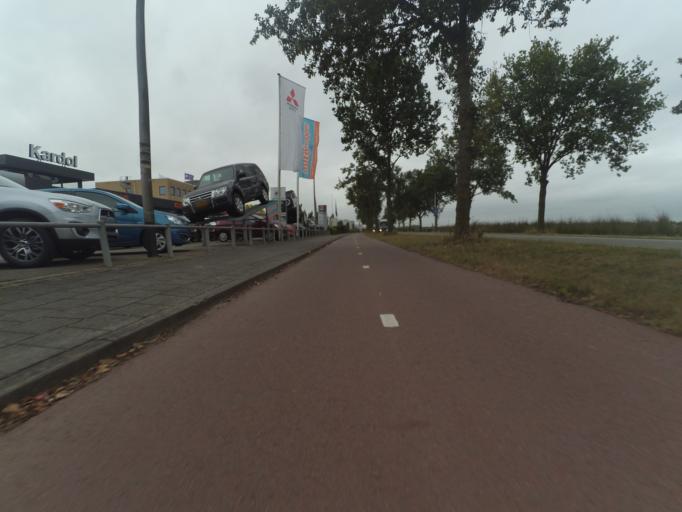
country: NL
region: Gelderland
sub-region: Gemeente Tiel
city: Tiel
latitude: 51.9129
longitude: 5.4256
